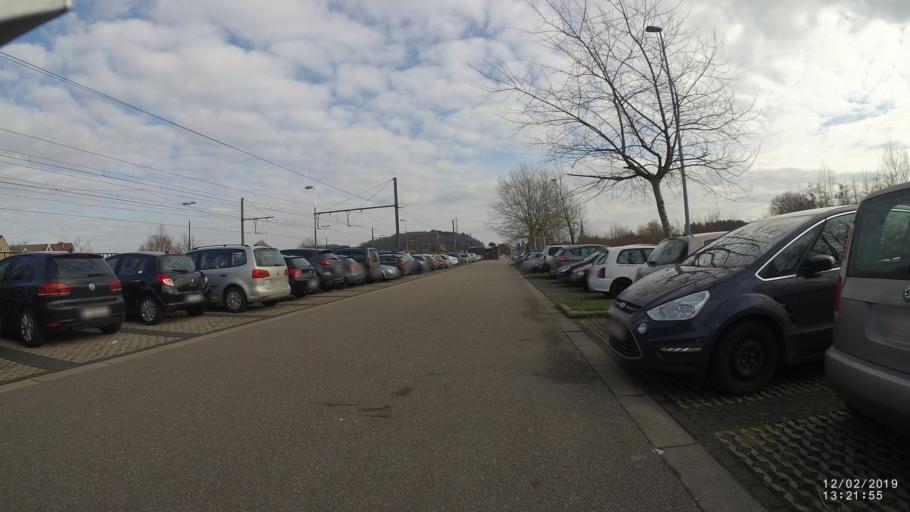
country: BE
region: Flanders
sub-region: Provincie Vlaams-Brabant
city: Scherpenheuvel-Zichem
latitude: 51.0097
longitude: 4.9448
